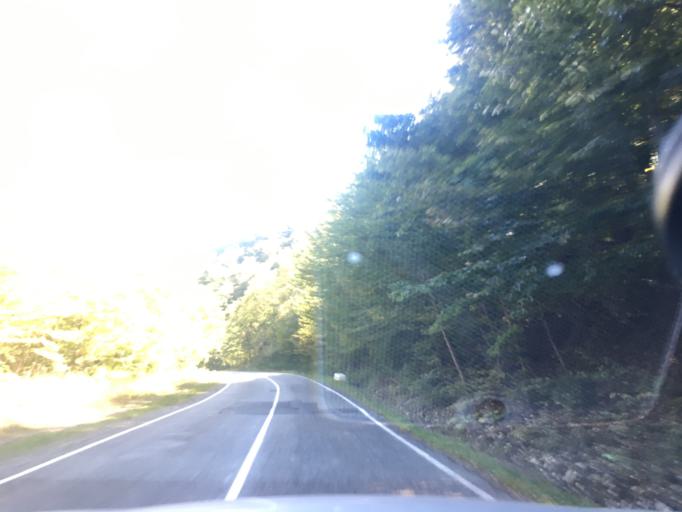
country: GE
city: Didi Lilo
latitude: 41.8784
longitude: 44.9116
